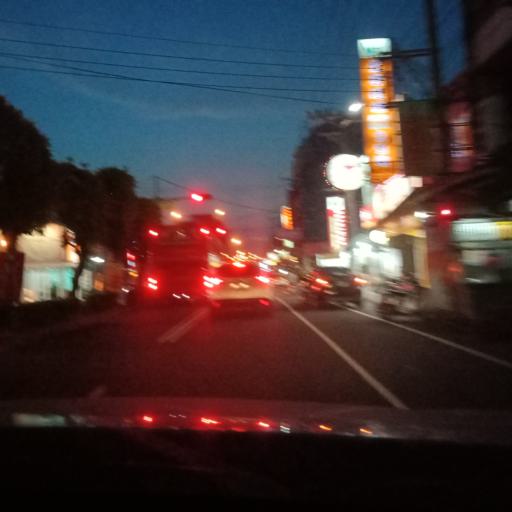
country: TW
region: Taiwan
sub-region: Hsinchu
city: Zhubei
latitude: 24.9022
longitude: 121.0484
